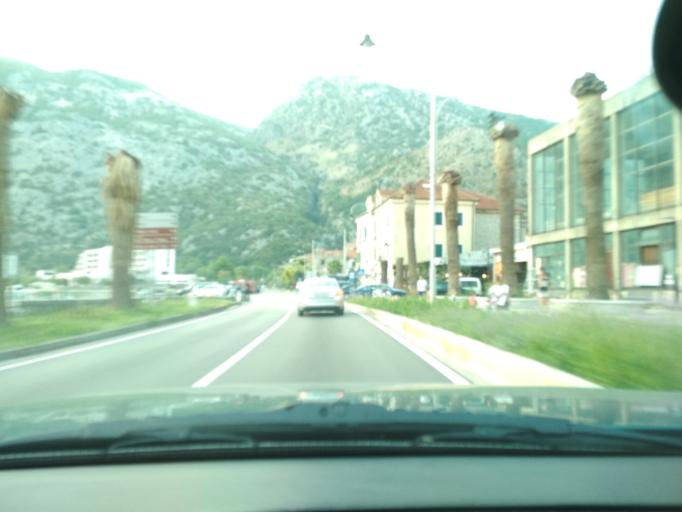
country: ME
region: Kotor
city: Risan
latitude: 42.5141
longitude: 18.6944
